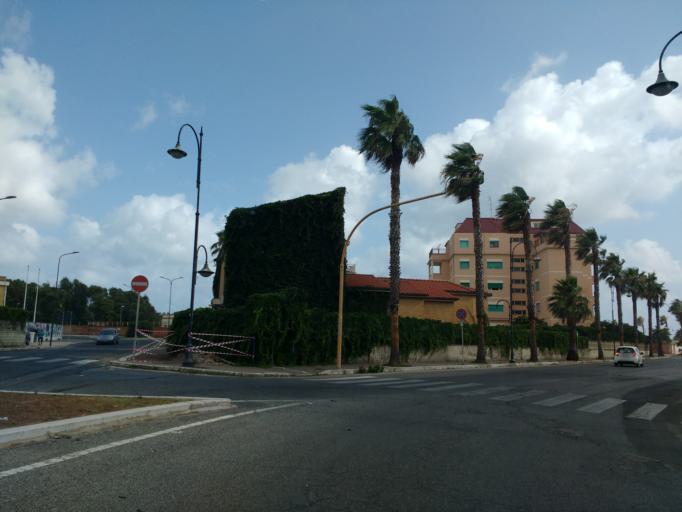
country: IT
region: Latium
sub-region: Citta metropolitana di Roma Capitale
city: Anzio
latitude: 41.4504
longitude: 12.6200
